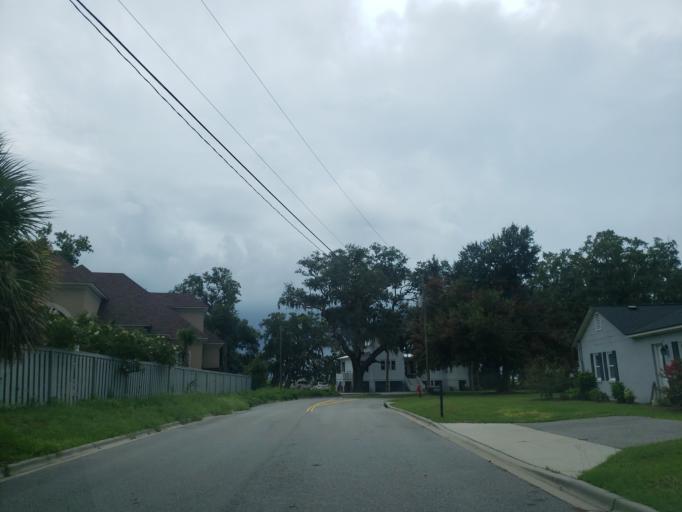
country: US
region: Georgia
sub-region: Chatham County
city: Wilmington Island
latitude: 31.9807
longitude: -80.9922
